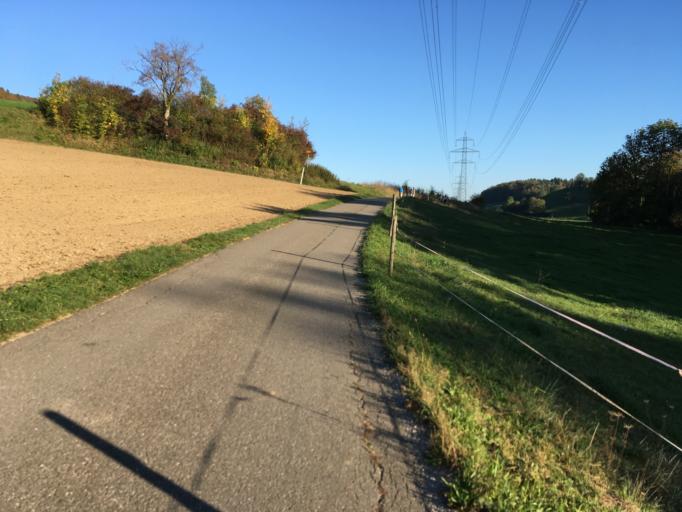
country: CH
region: Zurich
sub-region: Bezirk Buelach
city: Freienstein
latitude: 47.5358
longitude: 8.5873
